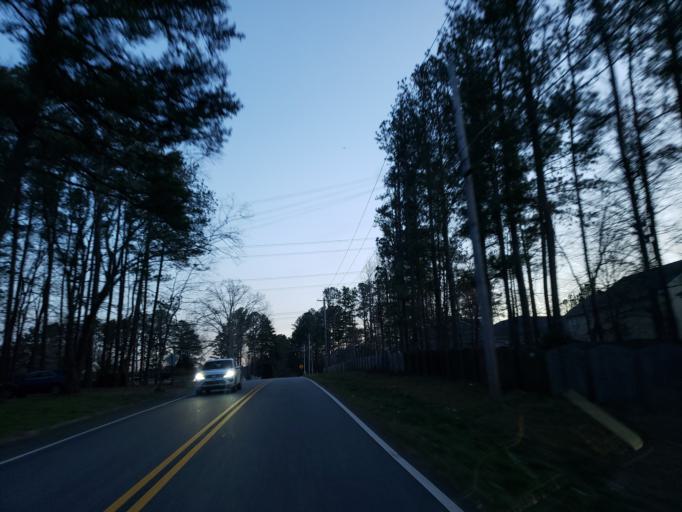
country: US
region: Georgia
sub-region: Cobb County
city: Kennesaw
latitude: 33.9968
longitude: -84.6346
